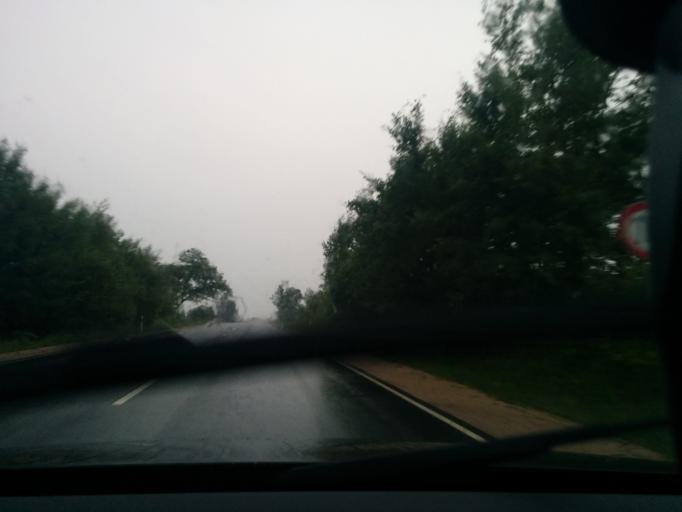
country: LV
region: Ikskile
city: Ikskile
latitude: 56.8716
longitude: 24.5396
